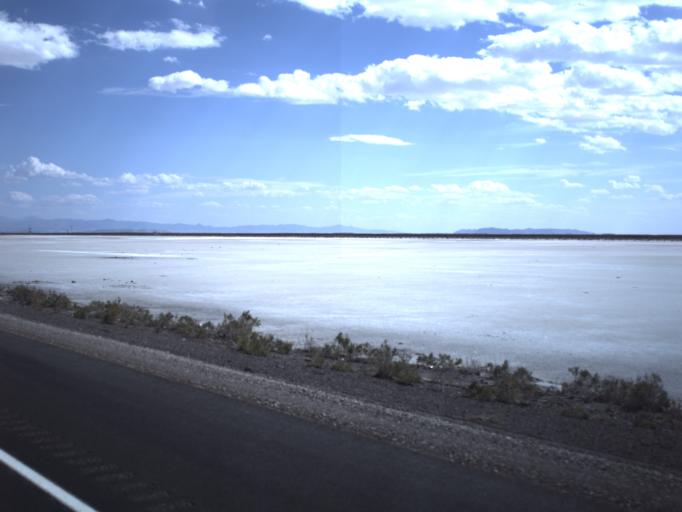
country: US
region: Utah
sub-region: Tooele County
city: Wendover
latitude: 40.7330
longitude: -113.5932
